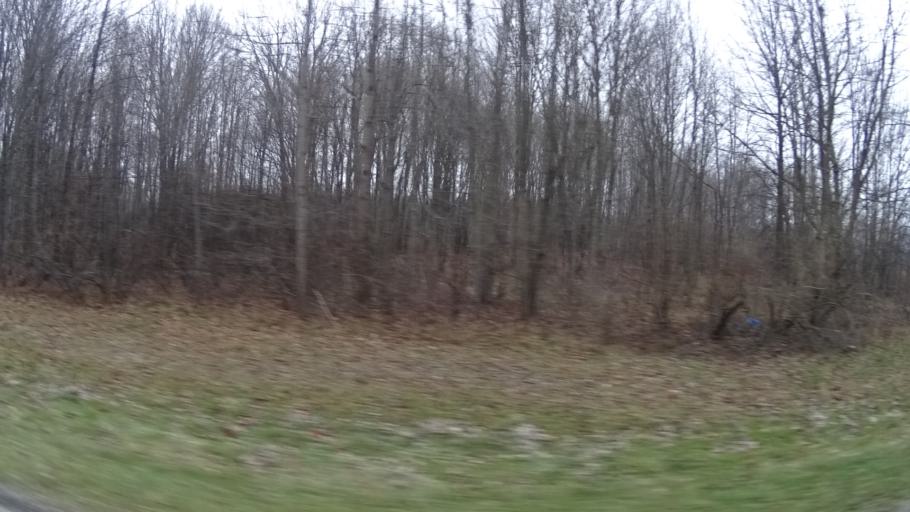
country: US
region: Ohio
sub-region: Lorain County
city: South Amherst
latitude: 41.3158
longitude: -82.2726
